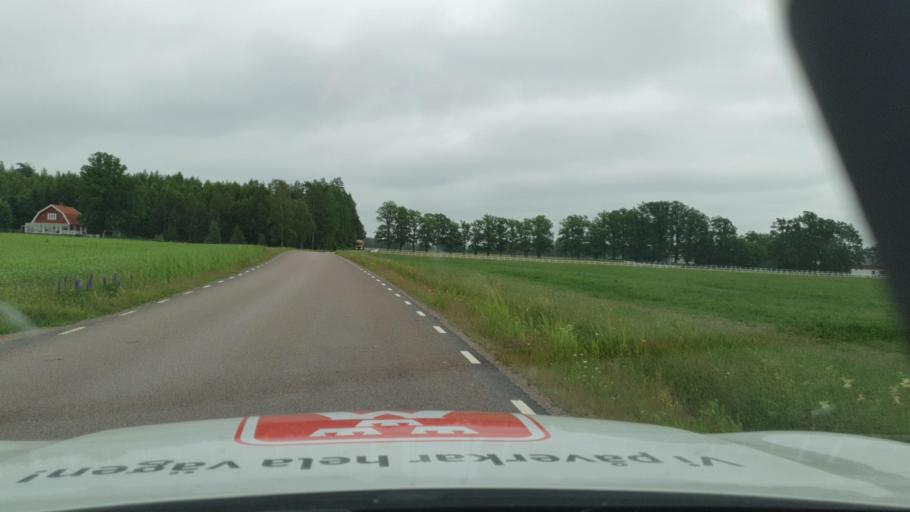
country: SE
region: Vaermland
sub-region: Kristinehamns Kommun
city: Kristinehamn
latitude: 59.4130
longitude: 13.8835
